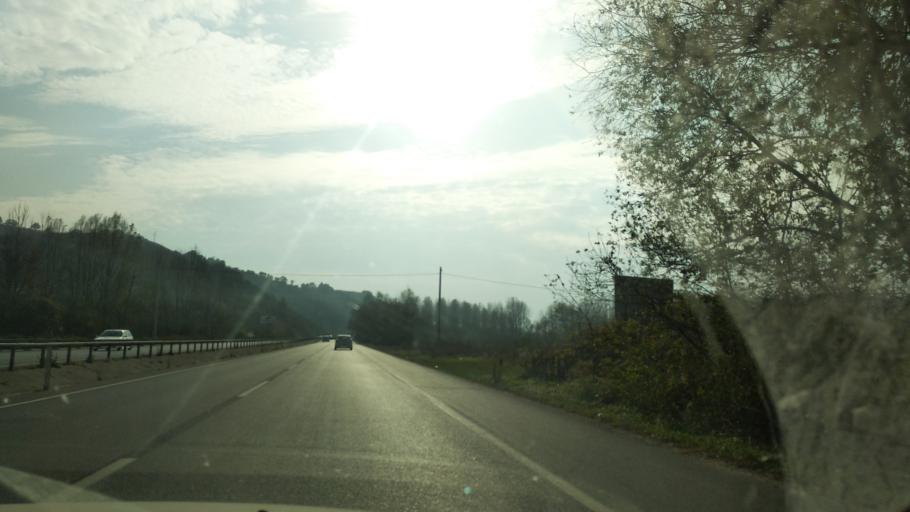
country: TR
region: Sakarya
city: Karasu
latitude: 41.0704
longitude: 30.6448
